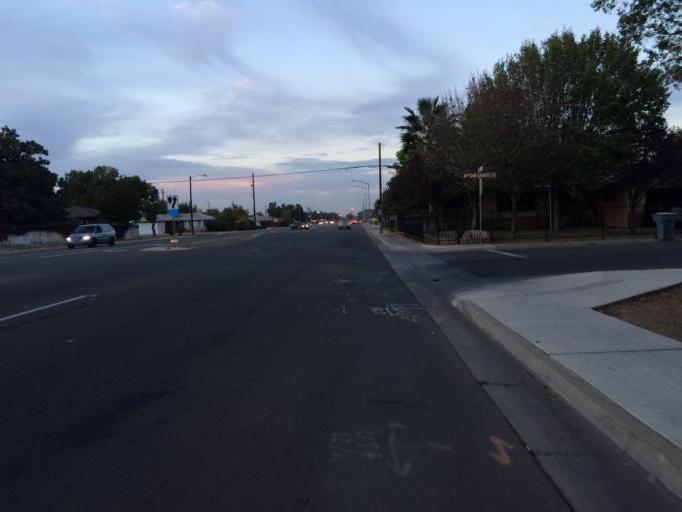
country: US
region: California
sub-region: Fresno County
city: Tarpey Village
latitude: 36.8040
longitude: -119.7272
